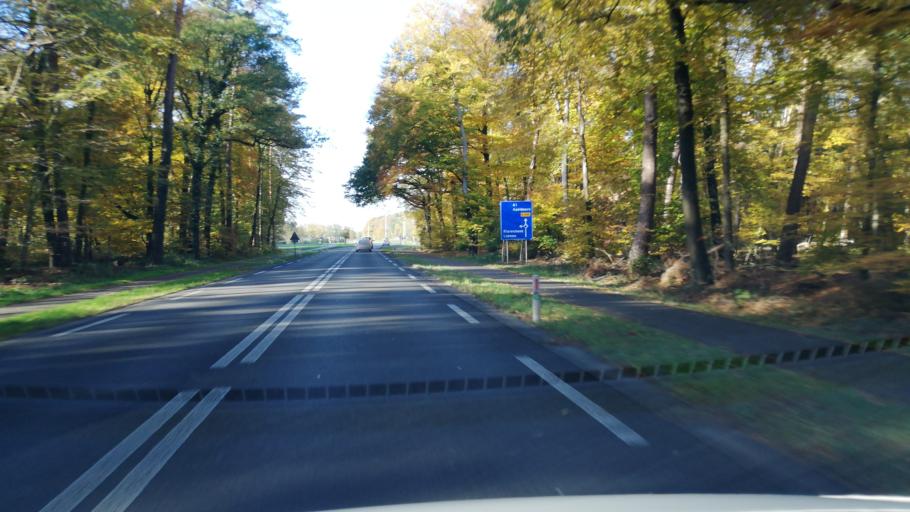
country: NL
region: Gelderland
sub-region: Gemeente Voorst
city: Voorst
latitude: 52.1855
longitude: 6.1120
